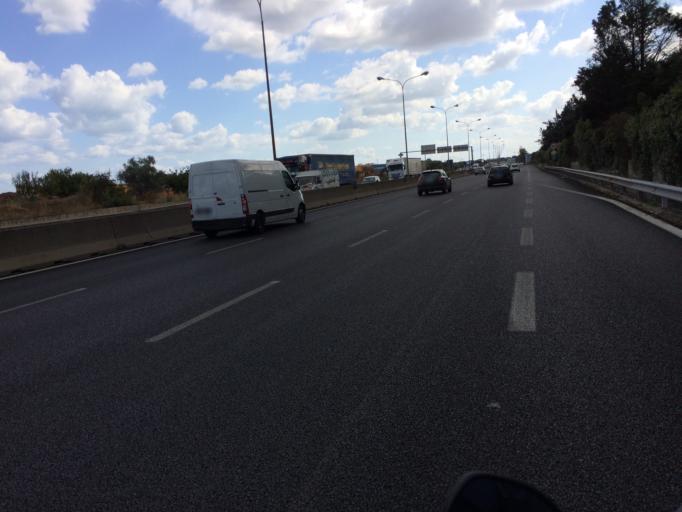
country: IT
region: Apulia
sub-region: Provincia di Bari
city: Bari
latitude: 41.0959
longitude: 16.8297
